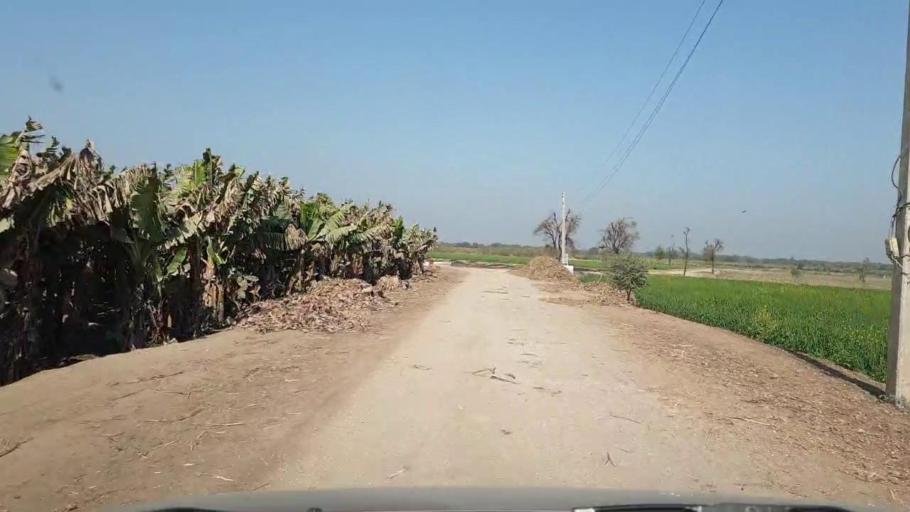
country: PK
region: Sindh
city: Tando Jam
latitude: 25.4371
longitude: 68.6183
